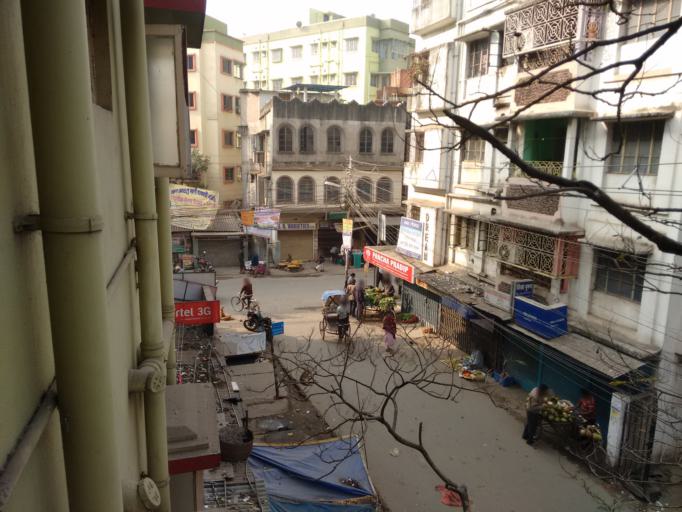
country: IN
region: West Bengal
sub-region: North 24 Parganas
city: Dam Dam
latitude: 22.6437
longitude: 88.4294
